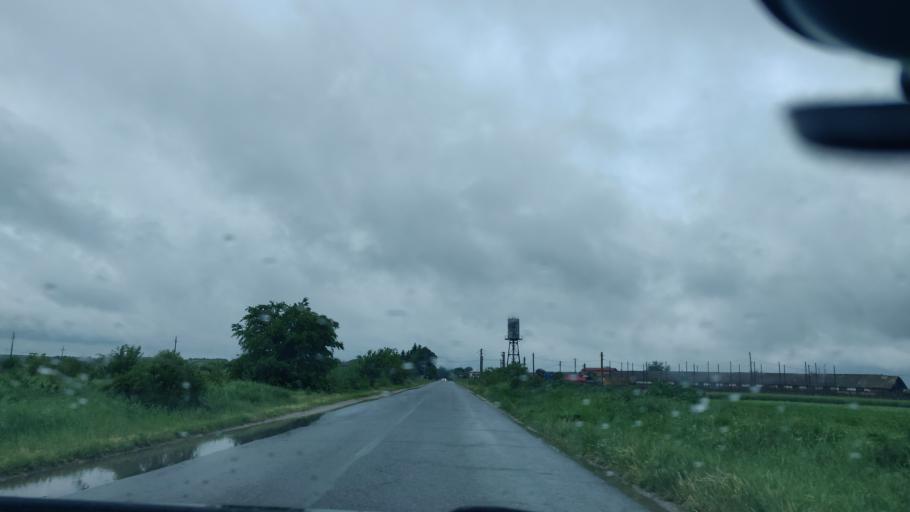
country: RO
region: Giurgiu
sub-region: Comuna Bulbucata
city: Bulbucata
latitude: 44.2726
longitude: 25.8340
